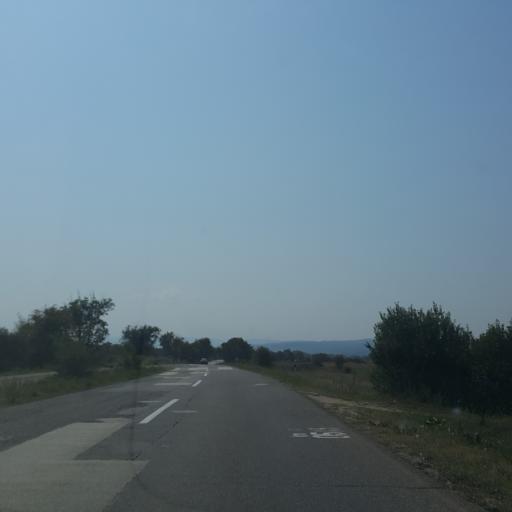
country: RS
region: Central Serbia
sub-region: Zajecarski Okrug
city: Knjazevac
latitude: 43.7043
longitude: 22.3025
